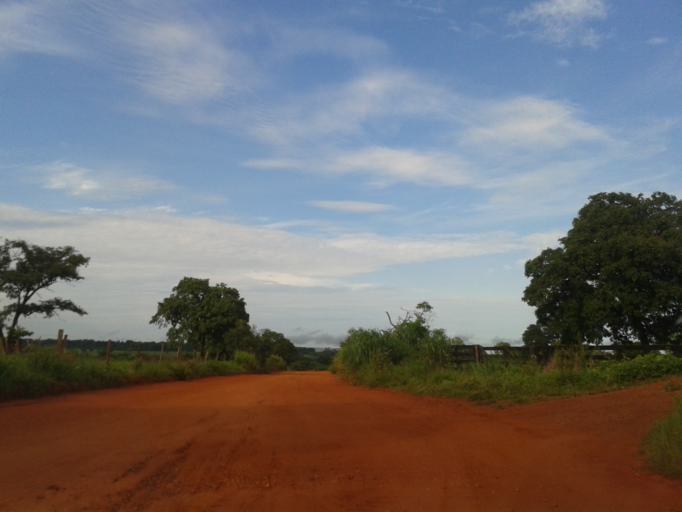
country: BR
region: Minas Gerais
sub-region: Santa Vitoria
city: Santa Vitoria
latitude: -19.1063
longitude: -50.5138
